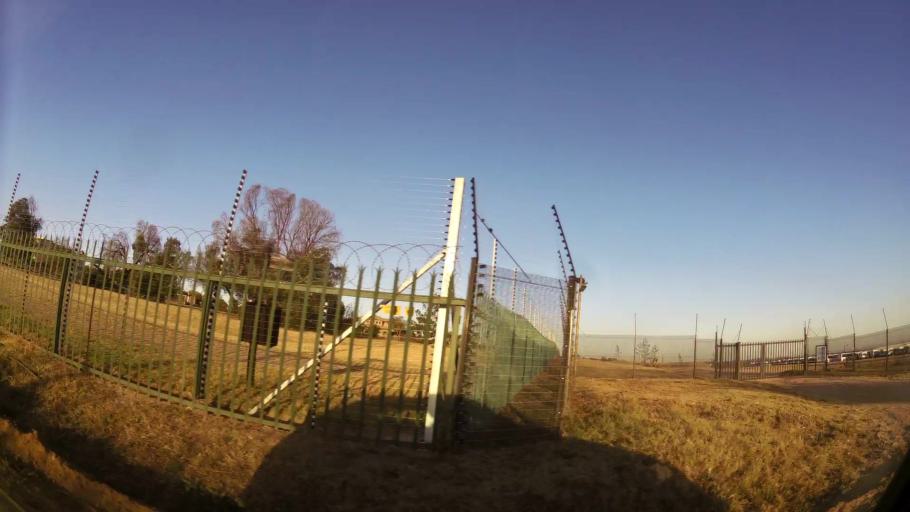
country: ZA
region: Gauteng
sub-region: City of Johannesburg Metropolitan Municipality
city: Diepsloot
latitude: -25.9436
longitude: 28.0392
